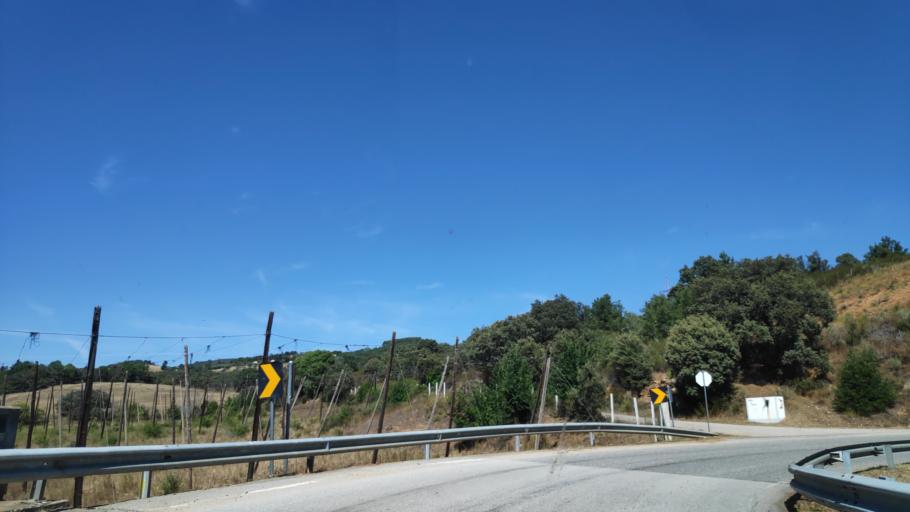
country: PT
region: Braganca
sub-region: Braganca Municipality
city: Braganca
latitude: 41.8295
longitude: -6.7517
